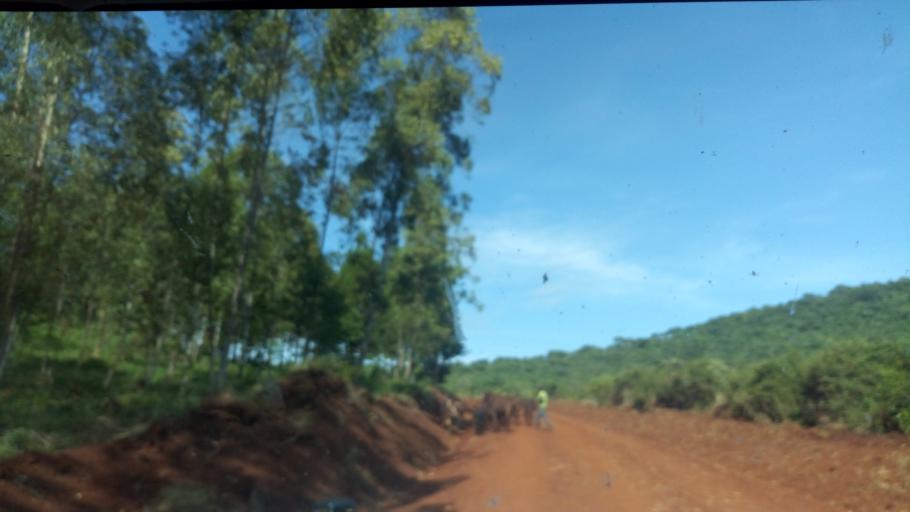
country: UG
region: Western Region
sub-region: Masindi District
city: Masindi
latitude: 1.6498
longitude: 31.7778
